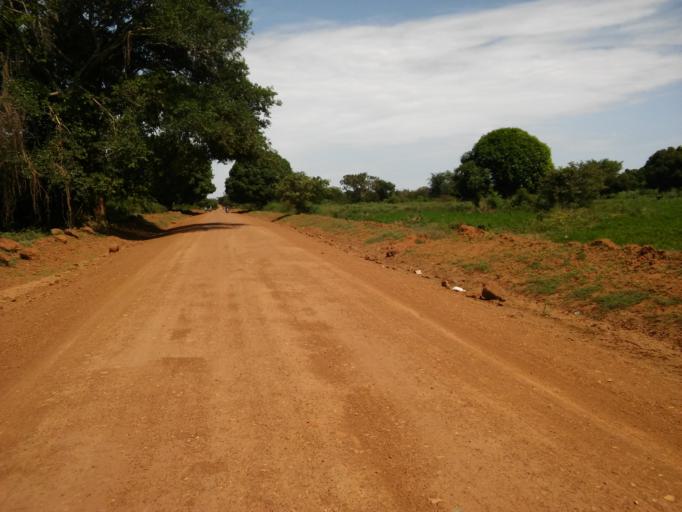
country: UG
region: Eastern Region
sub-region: Kumi District
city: Kumi
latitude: 1.4754
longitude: 33.8790
